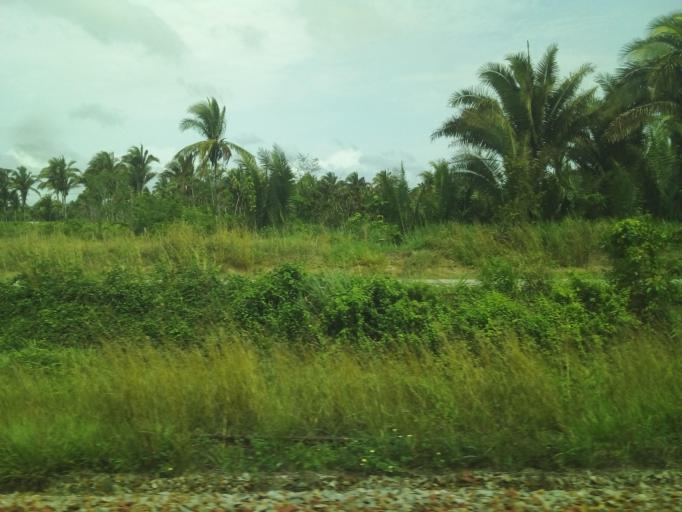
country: BR
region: Maranhao
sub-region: Arari
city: Arari
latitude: -3.5146
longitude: -44.6259
